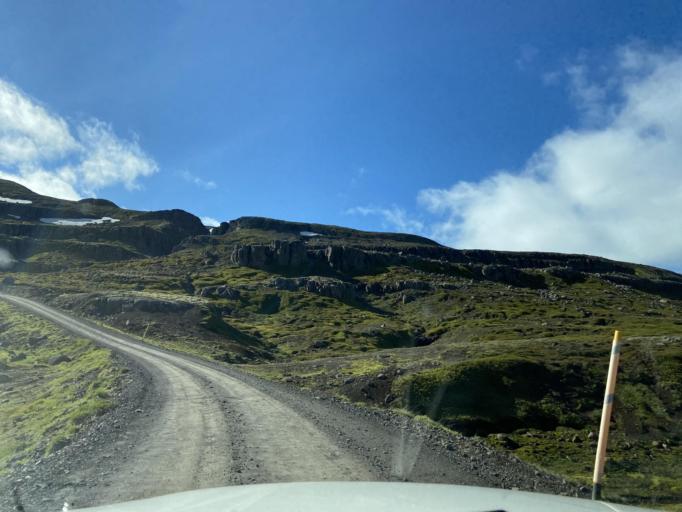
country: IS
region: East
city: Eskifjoerdur
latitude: 65.1788
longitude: -14.1002
